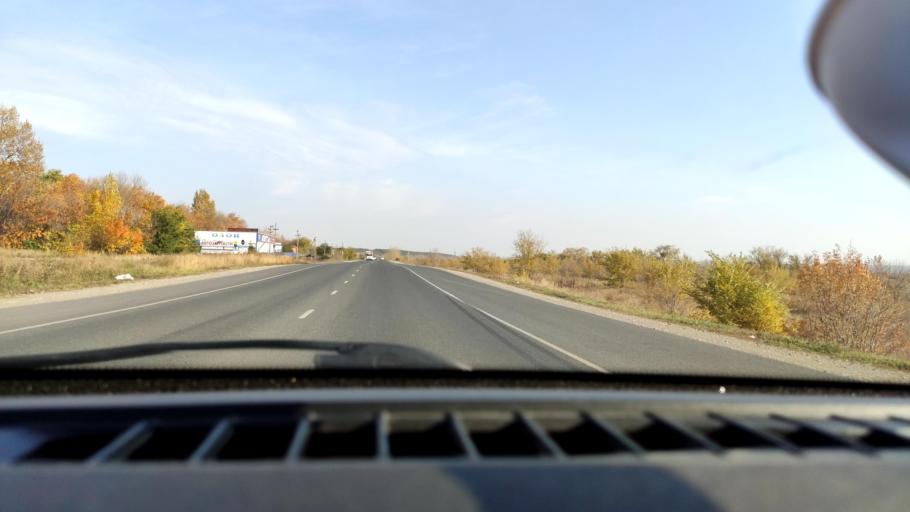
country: RU
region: Samara
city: Samara
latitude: 53.1243
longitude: 50.1839
